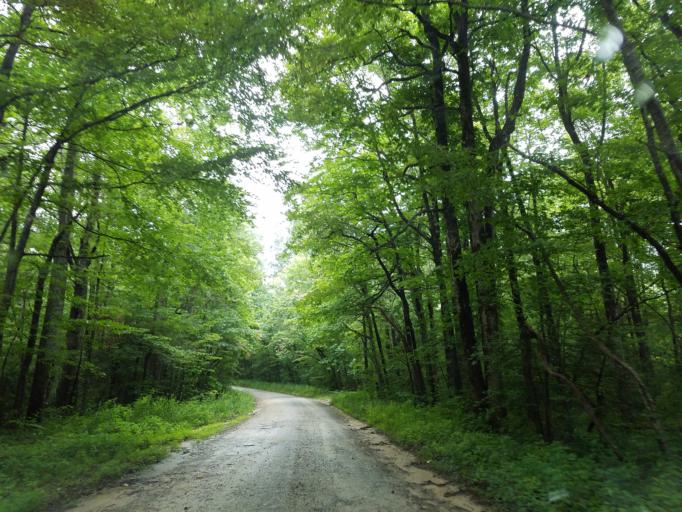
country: US
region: Georgia
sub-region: Lumpkin County
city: Dahlonega
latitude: 34.6445
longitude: -84.1582
